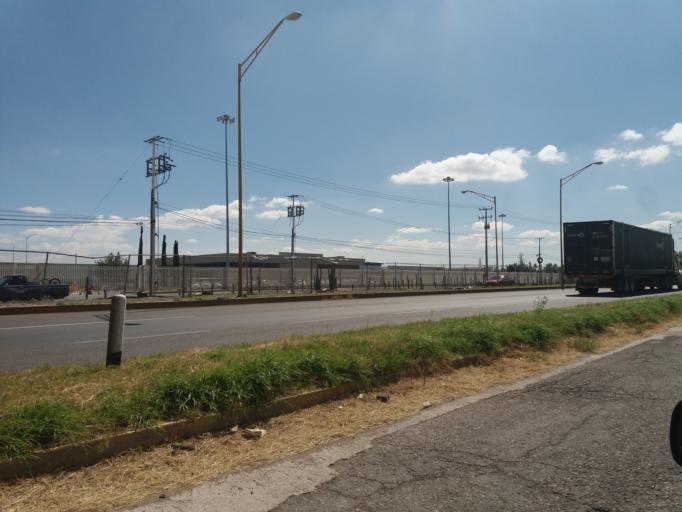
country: MX
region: Aguascalientes
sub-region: Aguascalientes
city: San Sebastian [Fraccionamiento]
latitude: 21.8061
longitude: -102.2845
